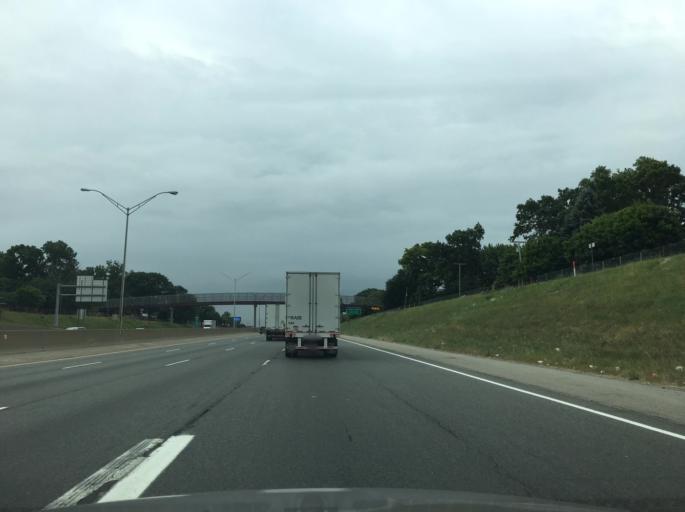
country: US
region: Michigan
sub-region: Oakland County
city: Hazel Park
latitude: 42.4727
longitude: -83.1109
